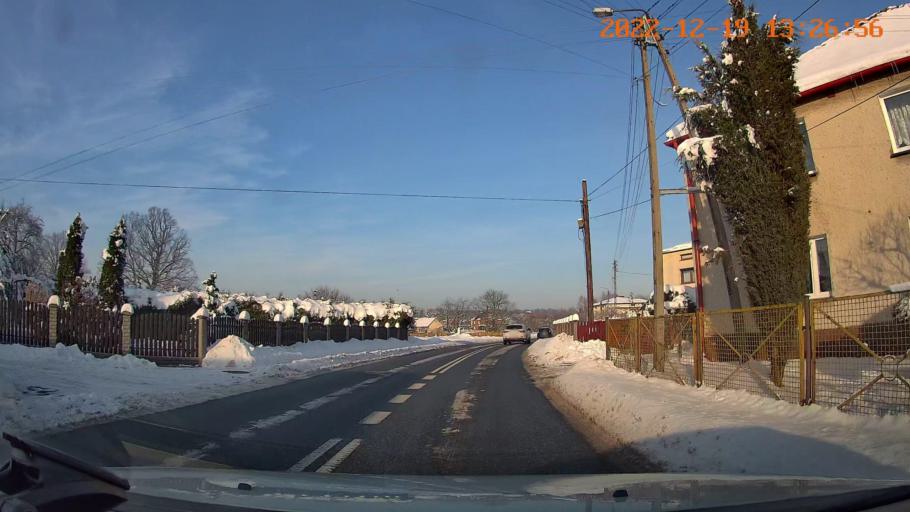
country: PL
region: Silesian Voivodeship
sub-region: Powiat bierunsko-ledzinski
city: Ledziny
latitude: 50.1043
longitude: 19.1364
